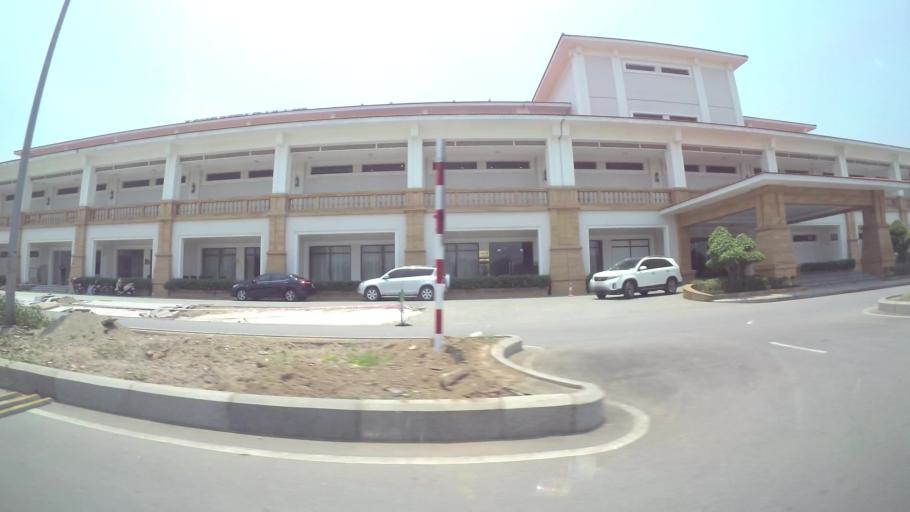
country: VN
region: Ha Noi
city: Trau Quy
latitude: 21.0384
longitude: 105.8961
